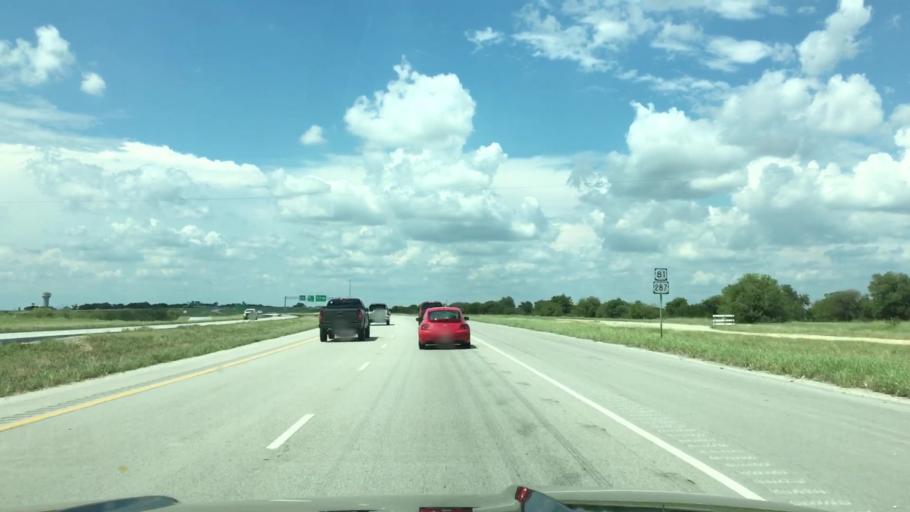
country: US
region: Texas
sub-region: Wise County
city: Rhome
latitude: 33.0391
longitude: -97.4550
